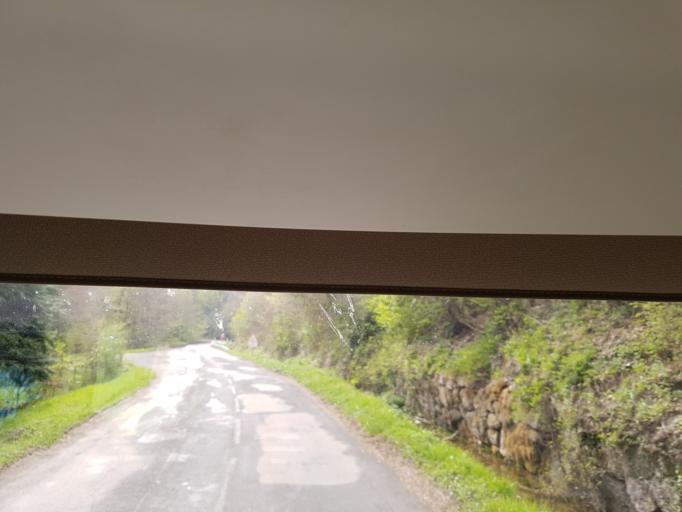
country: FR
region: Languedoc-Roussillon
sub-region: Departement de l'Aude
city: Quillan
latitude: 42.7762
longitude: 2.1520
